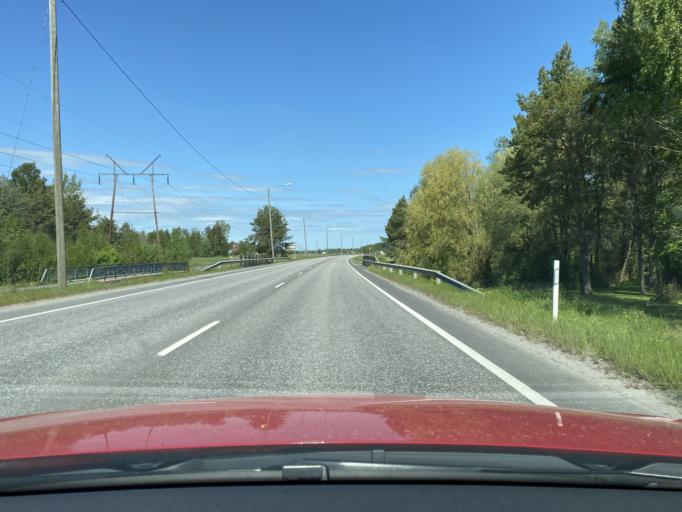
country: FI
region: Satakunta
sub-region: Rauma
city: Eura
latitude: 61.1266
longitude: 22.1270
